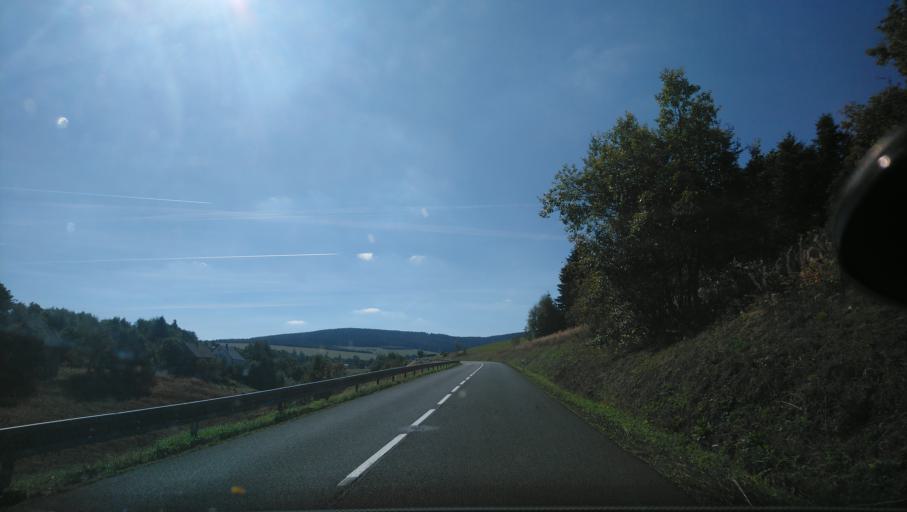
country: DE
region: Saxony
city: Kurort Oberwiesenthal
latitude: 50.4213
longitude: 12.9965
